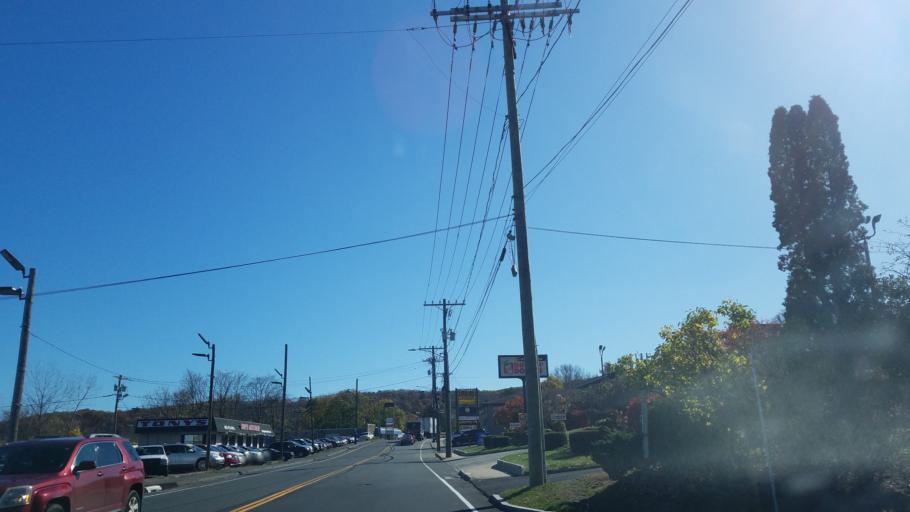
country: US
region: Connecticut
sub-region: New Haven County
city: Waterbury
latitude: 41.5404
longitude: -73.0216
